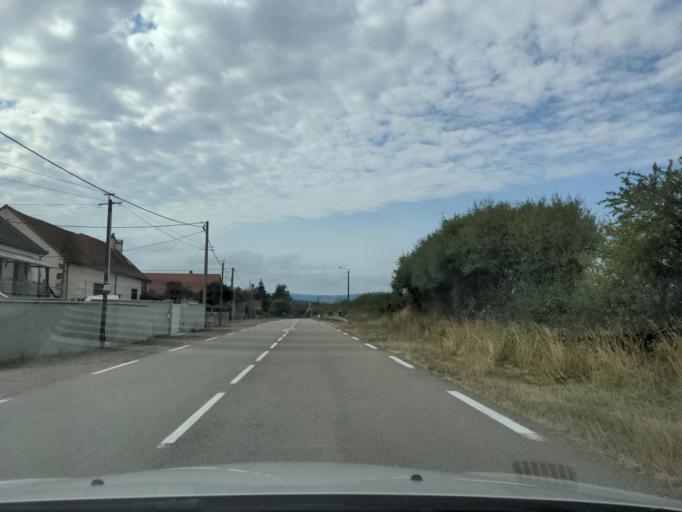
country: FR
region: Bourgogne
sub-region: Departement de Saone-et-Loire
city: Autun
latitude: 47.0092
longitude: 4.3209
